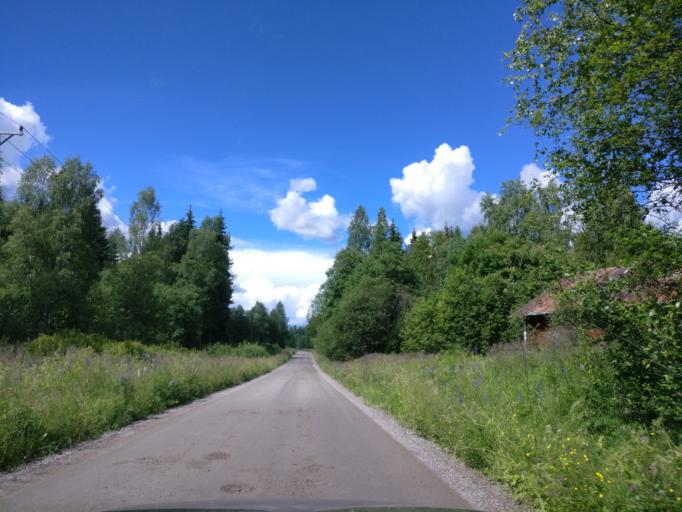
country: SE
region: Vaermland
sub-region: Hagfors Kommun
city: Hagfors
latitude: 60.0375
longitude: 13.6665
